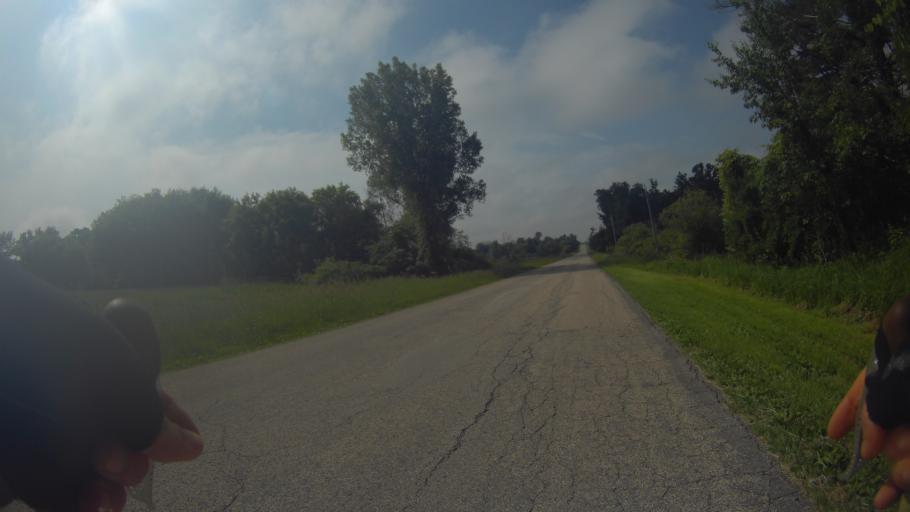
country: US
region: Wisconsin
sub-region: Dane County
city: Stoughton
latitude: 42.9480
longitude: -89.1810
